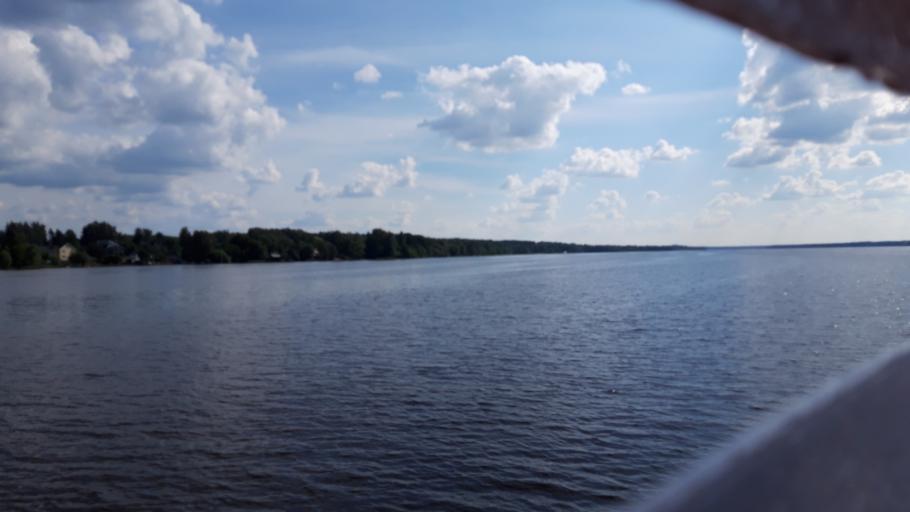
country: RU
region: Tverskaya
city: Konakovo
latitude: 56.6662
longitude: 36.6549
